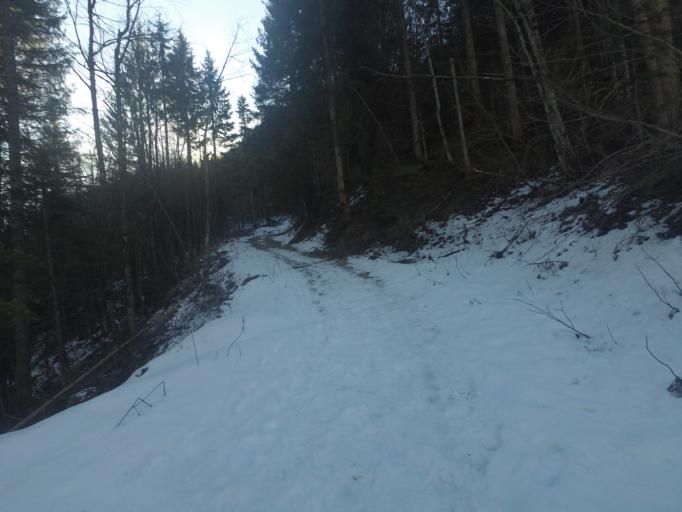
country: AT
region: Salzburg
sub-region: Politischer Bezirk Salzburg-Umgebung
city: Strobl
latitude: 47.6024
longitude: 13.4571
